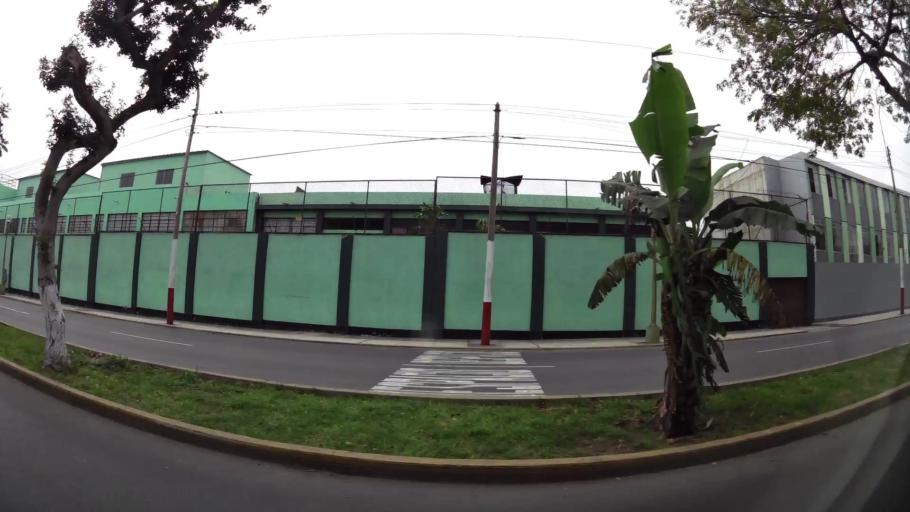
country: PE
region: Callao
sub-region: Callao
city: Callao
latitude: -12.0602
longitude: -77.1299
